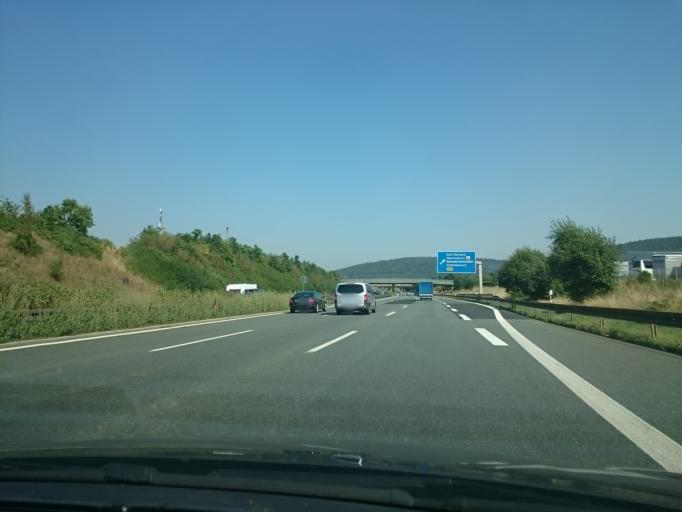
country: DE
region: Bavaria
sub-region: Upper Franconia
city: Himmelkron
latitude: 50.0504
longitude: 11.6176
